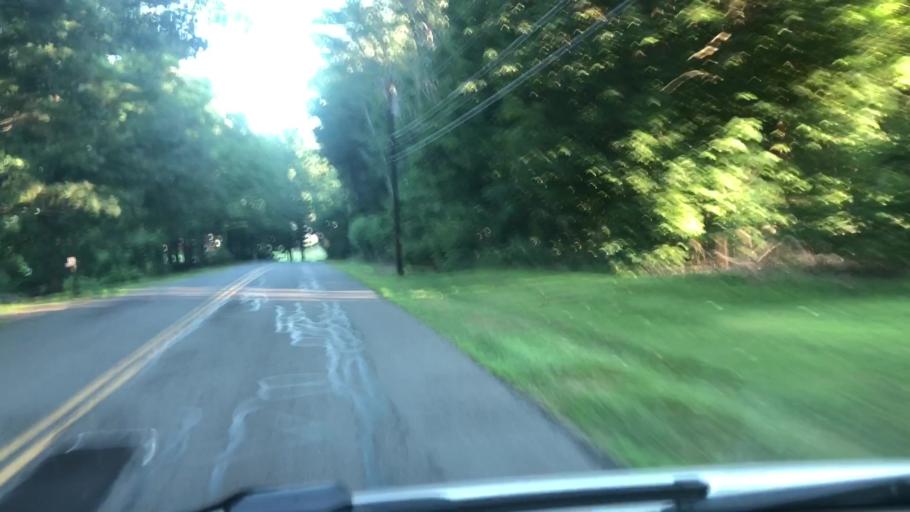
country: US
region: Massachusetts
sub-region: Hampshire County
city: Williamsburg
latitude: 42.3692
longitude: -72.7290
